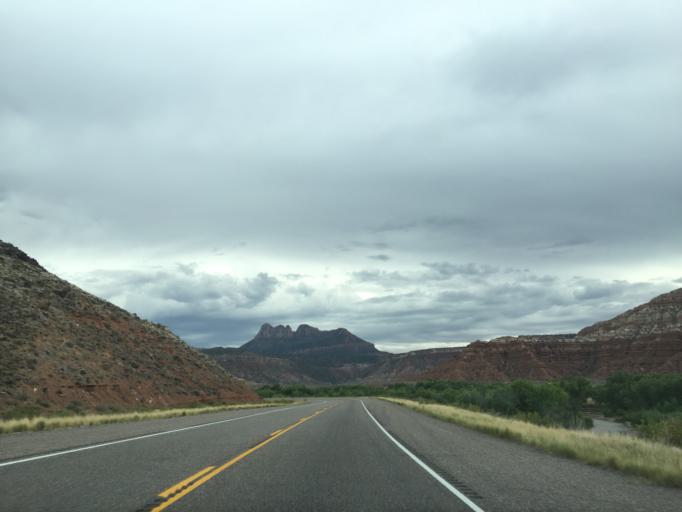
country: US
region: Utah
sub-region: Washington County
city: LaVerkin
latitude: 37.1763
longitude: -113.1151
